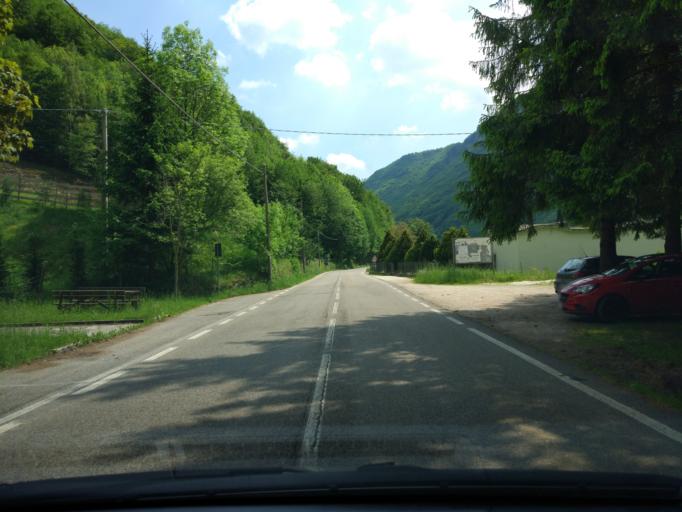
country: IT
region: Veneto
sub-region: Provincia di Verona
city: Selva di Progno
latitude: 45.6490
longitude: 11.1240
